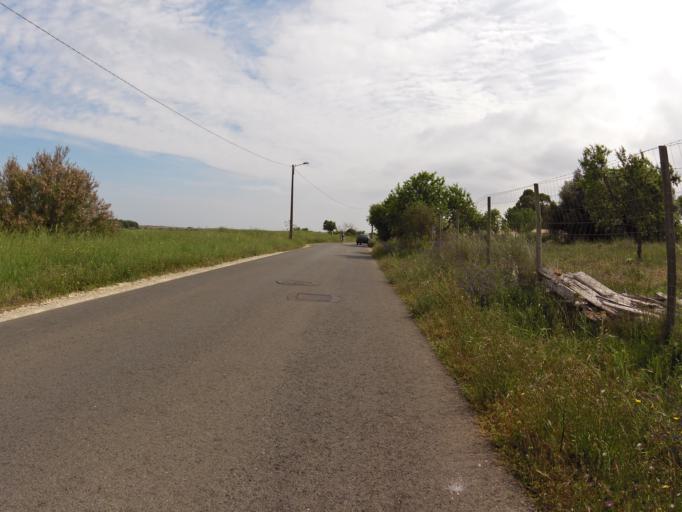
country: PT
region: Faro
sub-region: Silves
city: Armacao de Pera
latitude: 37.1094
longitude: -8.3495
